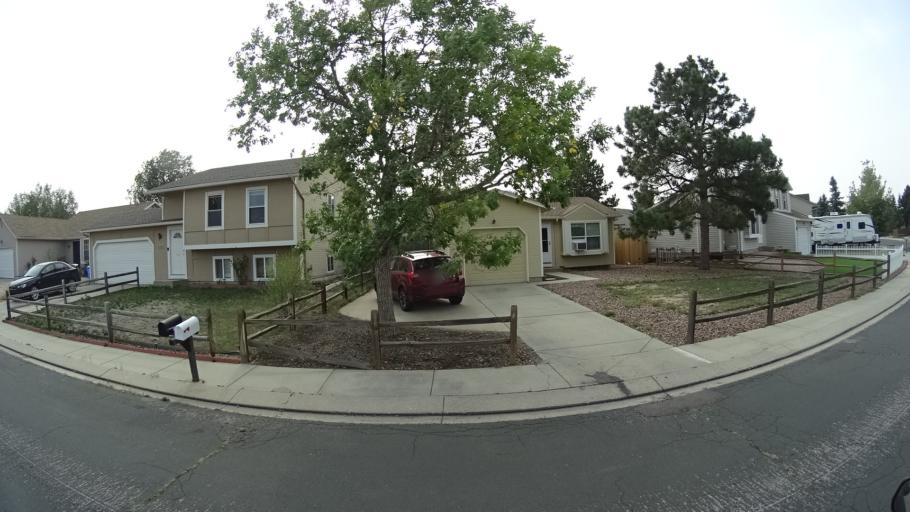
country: US
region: Colorado
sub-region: El Paso County
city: Stratmoor
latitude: 38.8071
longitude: -104.7499
